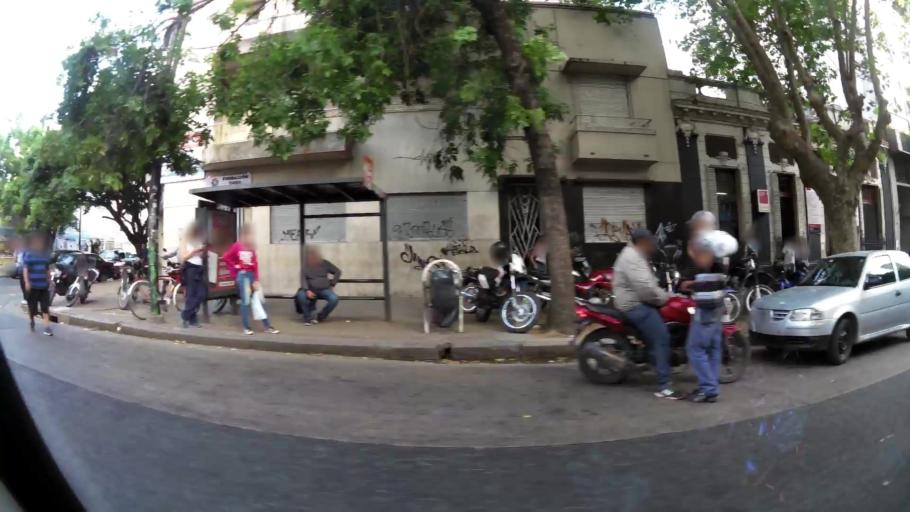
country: AR
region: Buenos Aires
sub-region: Partido de La Plata
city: La Plata
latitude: -34.9081
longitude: -57.9523
